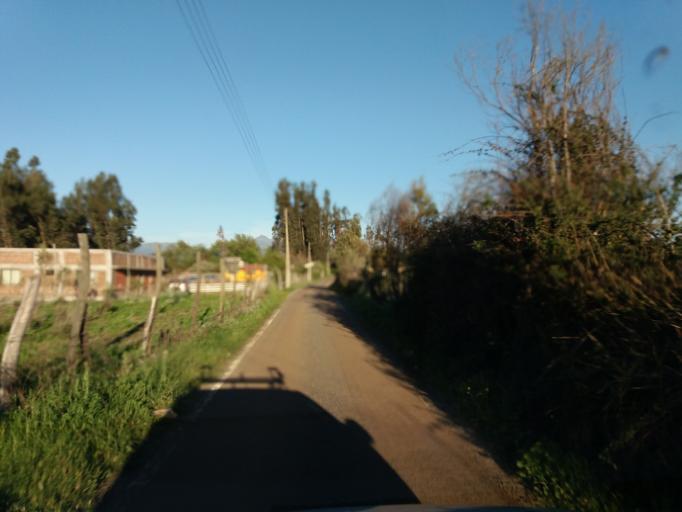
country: CL
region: Valparaiso
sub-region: Provincia de Quillota
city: Quillota
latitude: -32.9132
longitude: -71.3396
